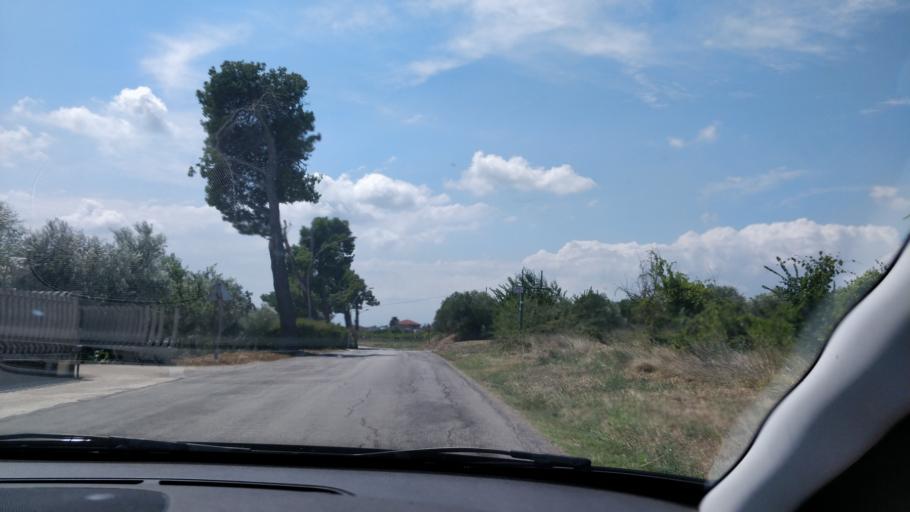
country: IT
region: Abruzzo
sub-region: Provincia di Chieti
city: Torrevecchia
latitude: 42.4156
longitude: 14.2292
